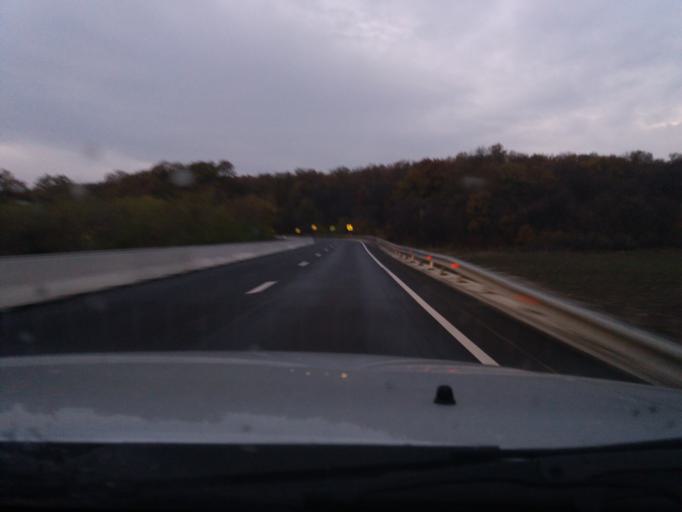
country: RO
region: Hunedoara
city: Berca
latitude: 45.6251
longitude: 22.9891
